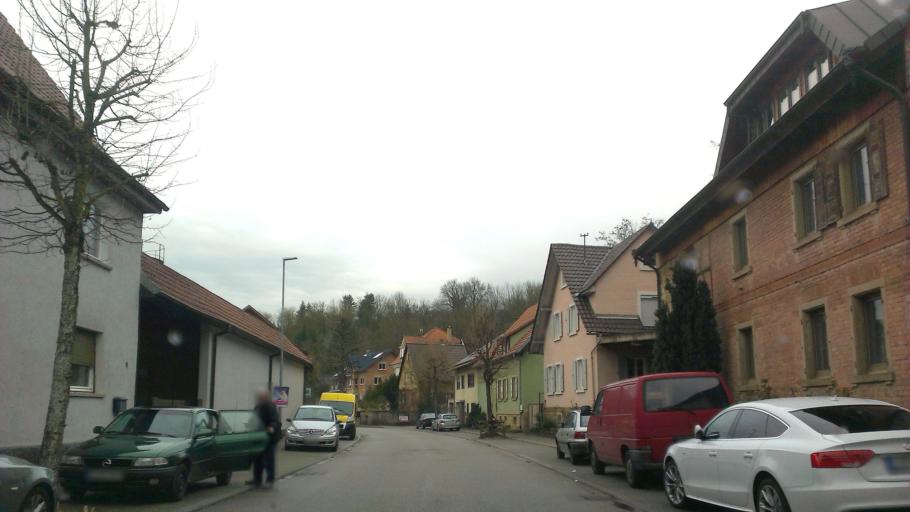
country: DE
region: Baden-Wuerttemberg
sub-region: Karlsruhe Region
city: Zaisenhausen
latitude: 49.1040
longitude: 8.7517
